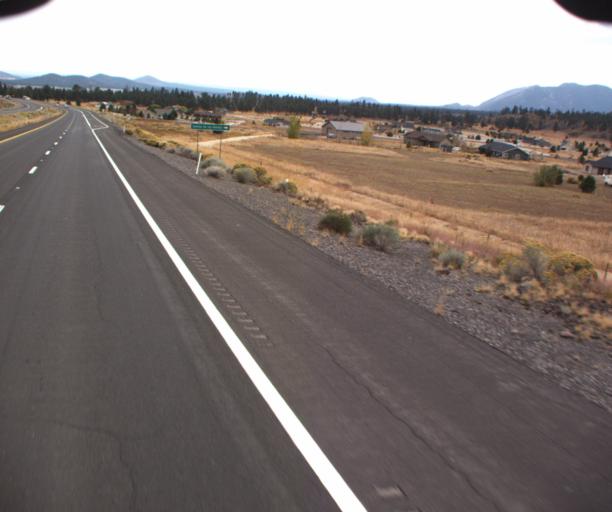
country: US
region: Arizona
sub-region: Coconino County
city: Flagstaff
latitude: 35.3472
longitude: -111.5630
